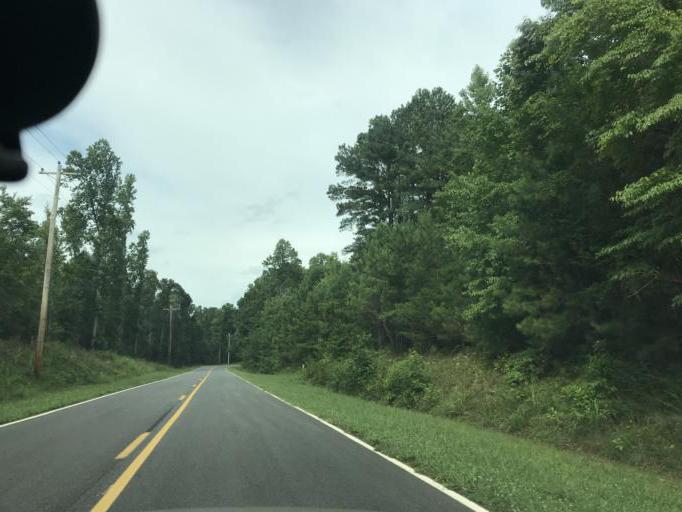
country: US
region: Georgia
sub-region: Dawson County
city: Dawsonville
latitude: 34.3253
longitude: -84.1906
